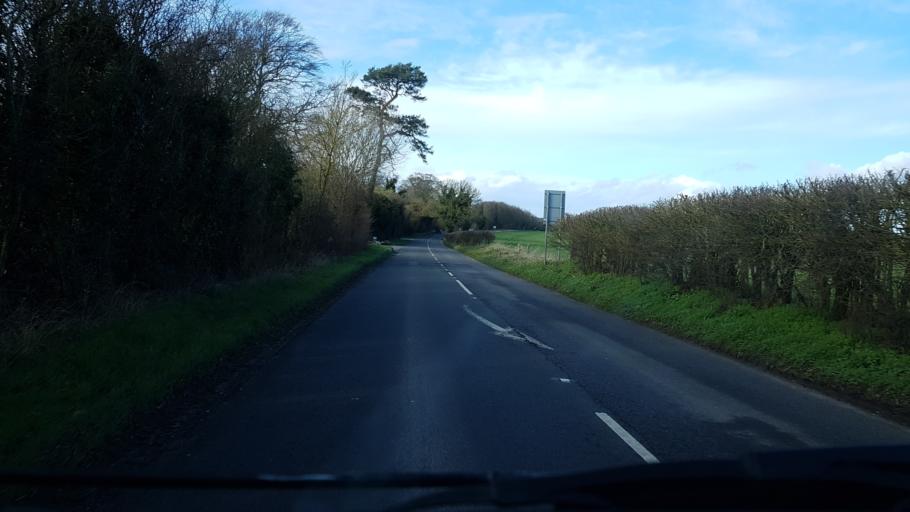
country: GB
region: England
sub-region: Wiltshire
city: Avebury
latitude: 51.4535
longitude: -1.8568
